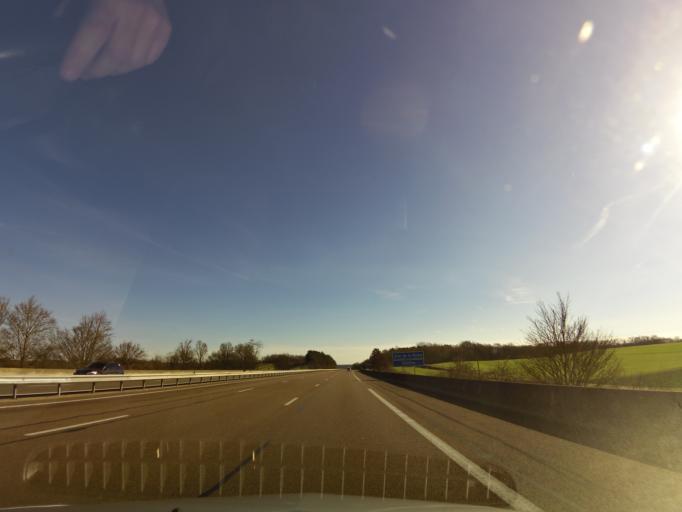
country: FR
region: Bourgogne
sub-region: Departement de l'Yonne
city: Fleury-la-Vallee
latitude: 47.8748
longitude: 3.4781
